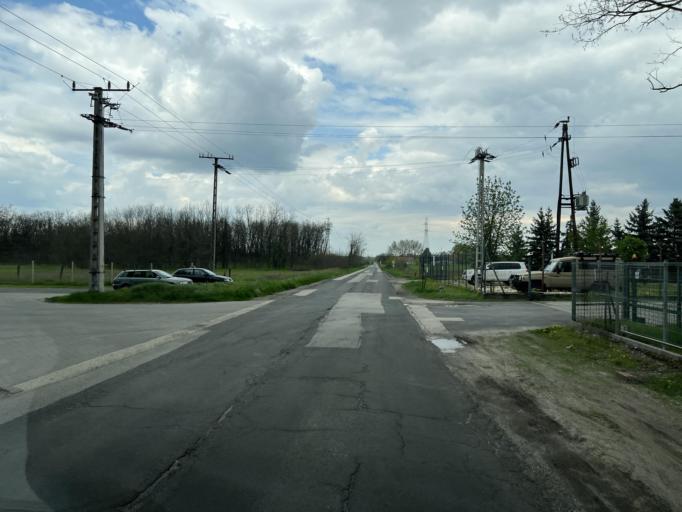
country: HU
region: Pest
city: Hernad
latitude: 47.1799
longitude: 19.4224
